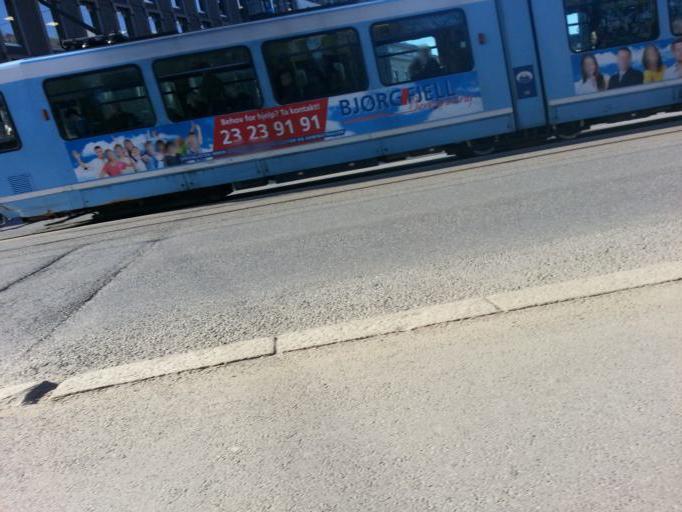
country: NO
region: Oslo
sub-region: Oslo
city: Oslo
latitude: 59.9155
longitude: 10.7247
